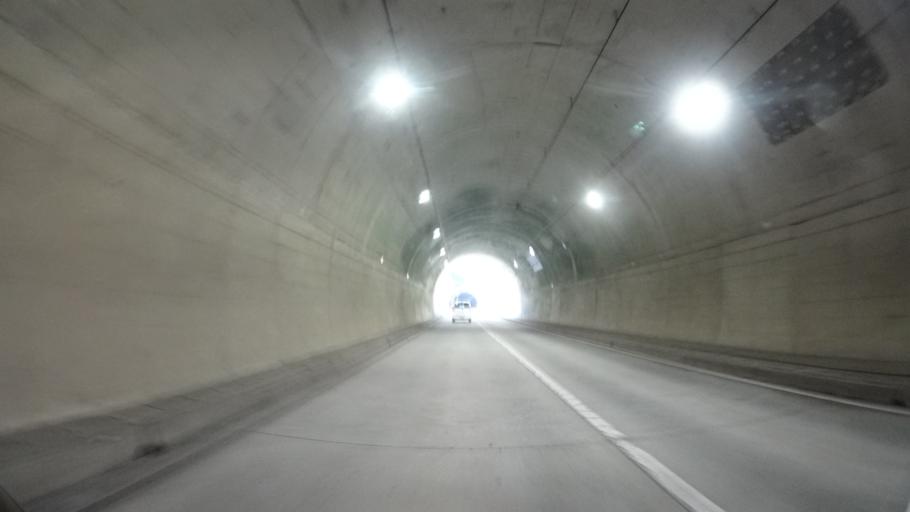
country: JP
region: Ehime
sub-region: Nishiuwa-gun
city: Ikata-cho
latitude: 33.4305
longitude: 132.2118
